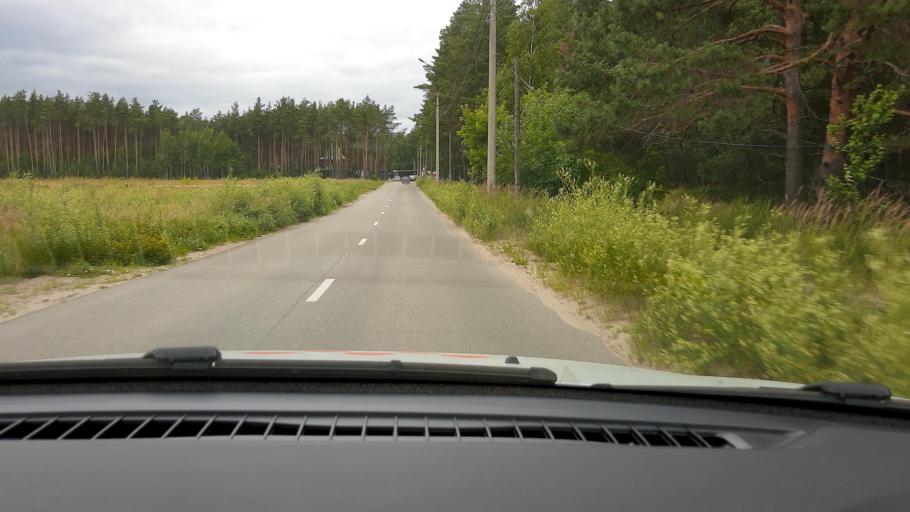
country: RU
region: Nizjnij Novgorod
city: Pyra
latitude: 56.2404
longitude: 43.3758
